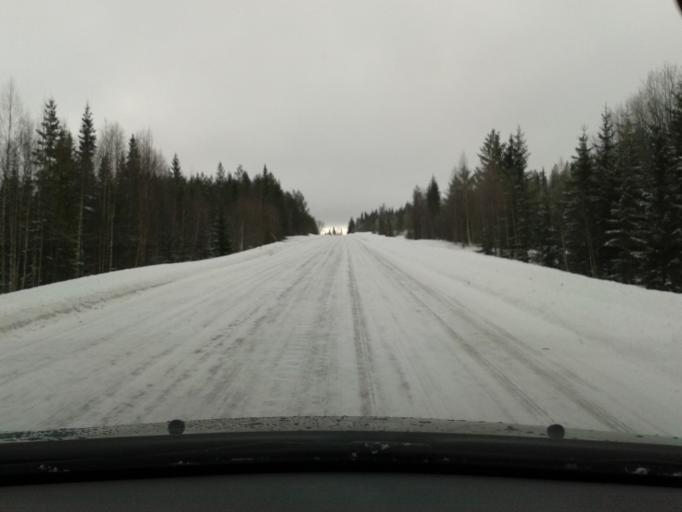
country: SE
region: Vaesterbotten
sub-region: Vilhelmina Kommun
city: Sjoberg
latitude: 64.8157
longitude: 15.9700
